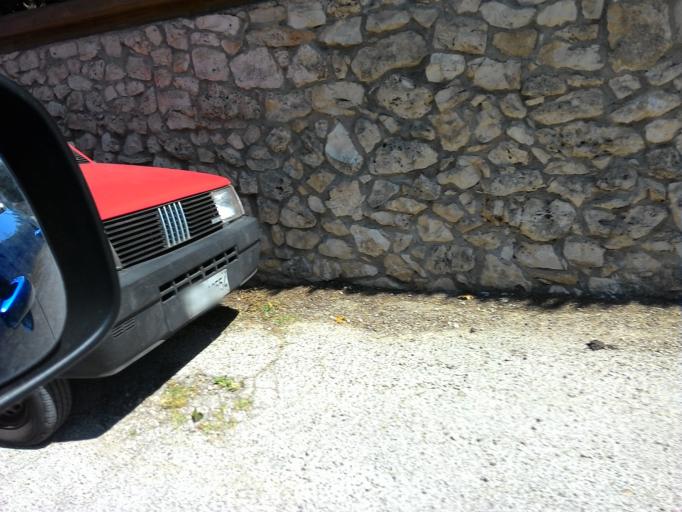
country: IT
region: Apulia
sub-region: Provincia di Bari
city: Putignano
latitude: 40.8365
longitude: 17.1443
